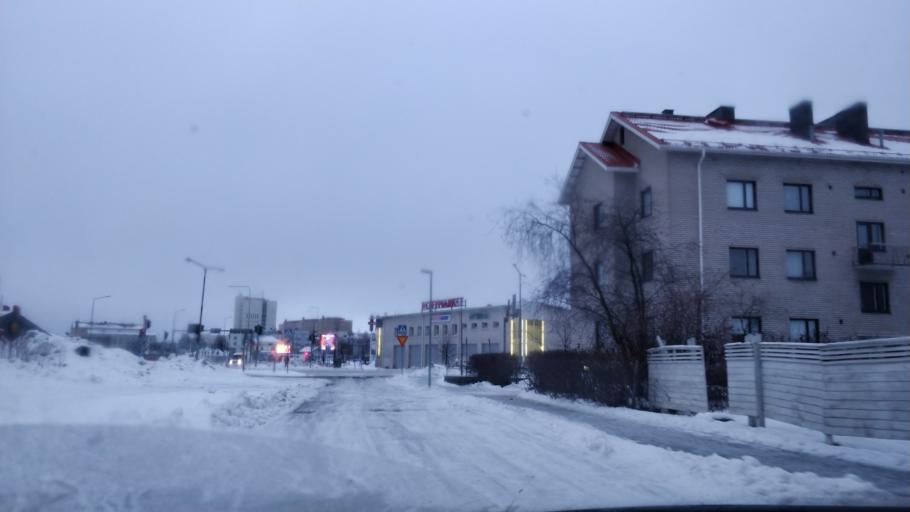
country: FI
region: Lapland
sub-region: Kemi-Tornio
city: Kemi
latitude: 65.7411
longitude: 24.5638
